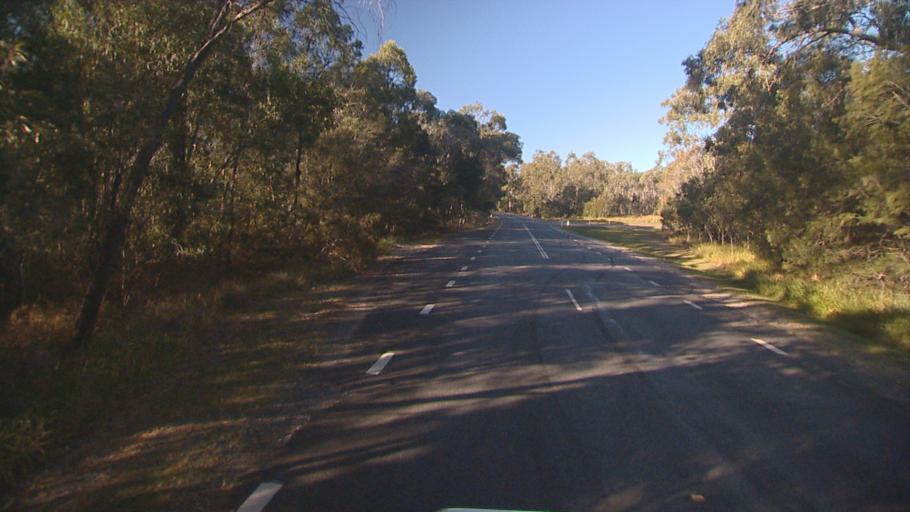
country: AU
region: Queensland
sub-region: Logan
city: Chambers Flat
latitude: -27.7796
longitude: 153.0703
